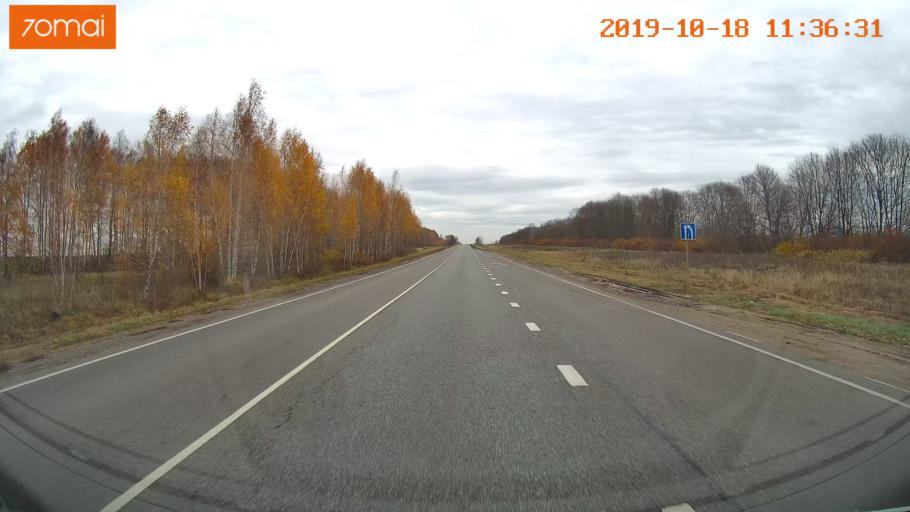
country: RU
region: Rjazan
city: Oktyabr'skiy
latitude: 54.1417
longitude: 38.8088
